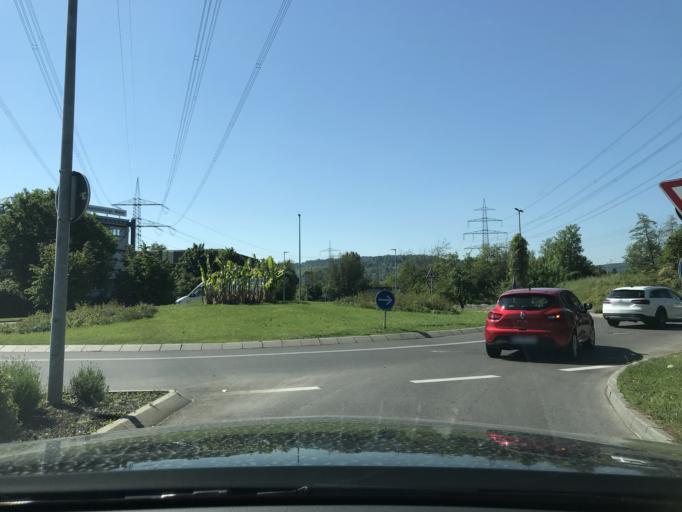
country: DE
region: Baden-Wuerttemberg
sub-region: Regierungsbezirk Stuttgart
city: Weinstadt-Endersbach
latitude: 48.8133
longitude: 9.3799
